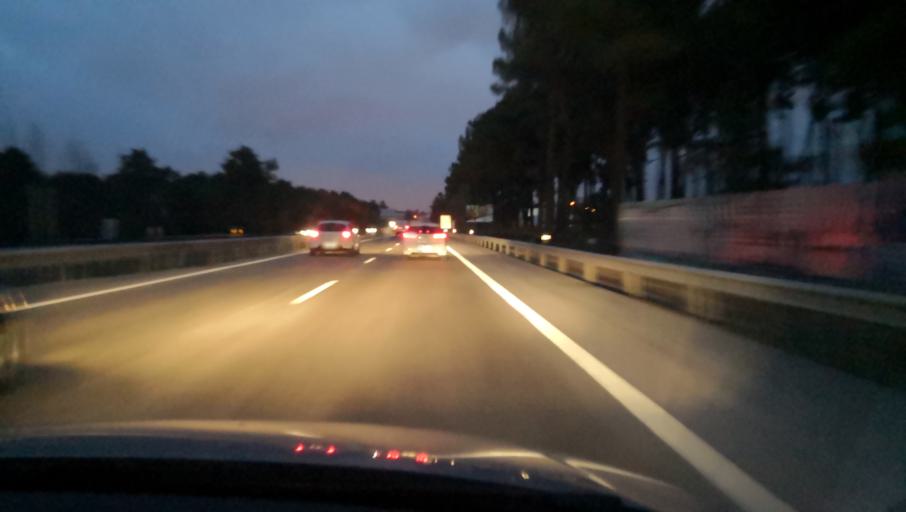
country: PT
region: Setubal
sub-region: Barreiro
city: Santo Antonio da Charneca
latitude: 38.6120
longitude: -9.0259
